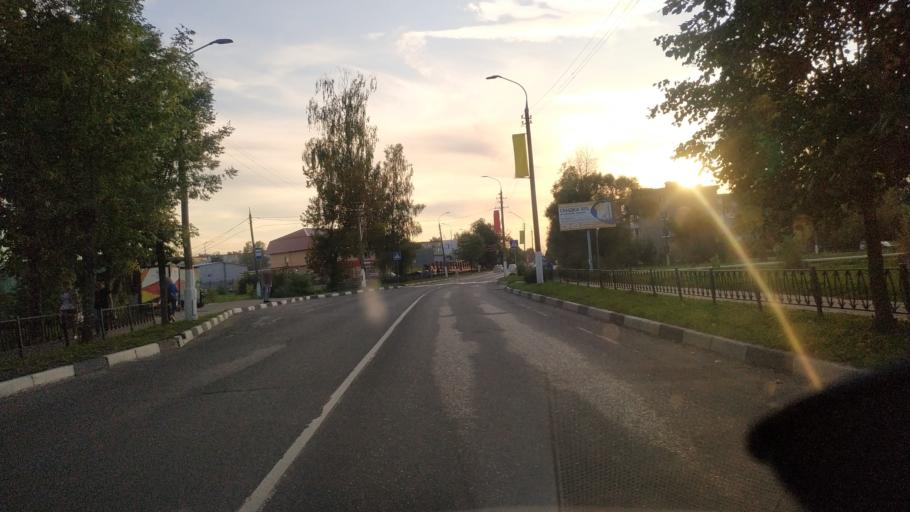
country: RU
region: Moskovskaya
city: Roshal'
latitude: 55.6633
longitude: 39.8581
